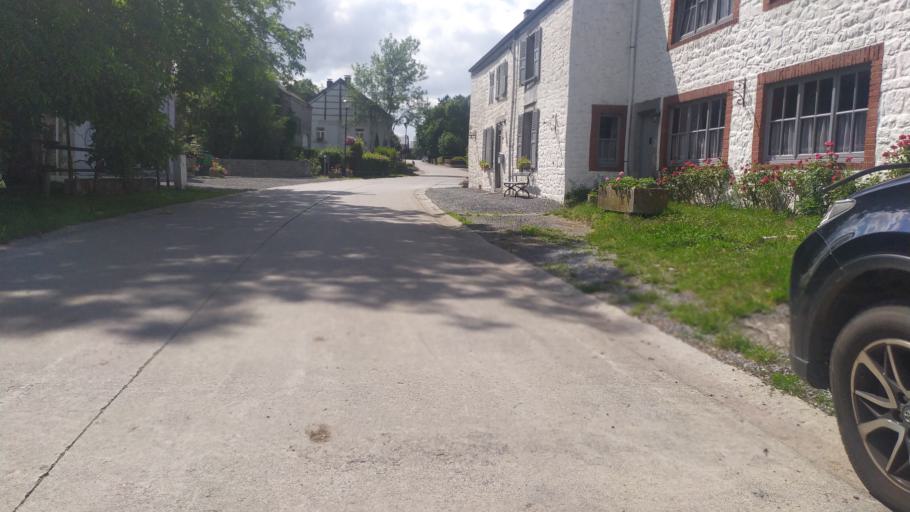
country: BE
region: Wallonia
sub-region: Province du Luxembourg
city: Wellin
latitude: 50.0682
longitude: 5.0714
